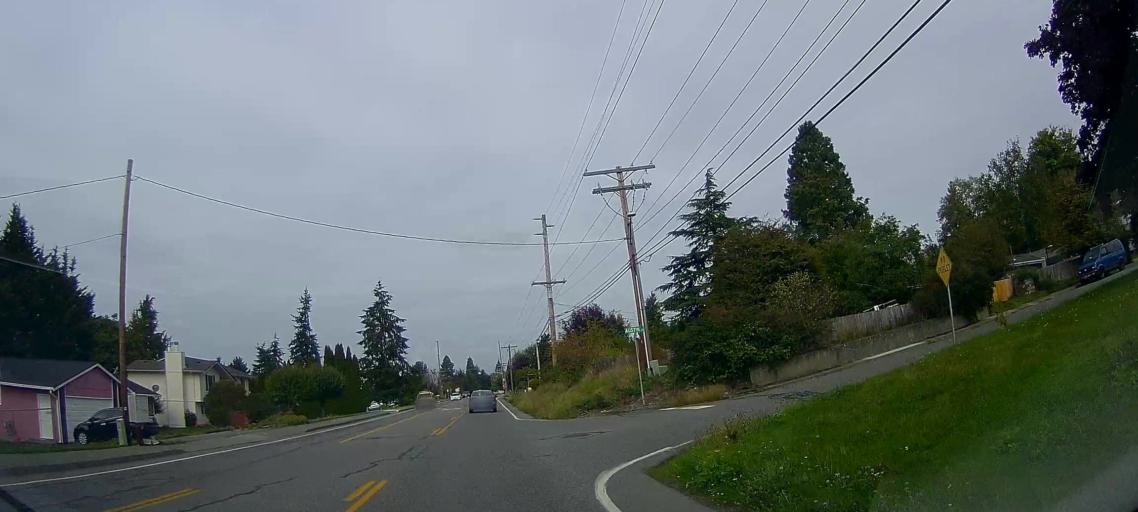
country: US
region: Washington
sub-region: Skagit County
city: Mount Vernon
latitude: 48.4408
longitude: -122.3132
